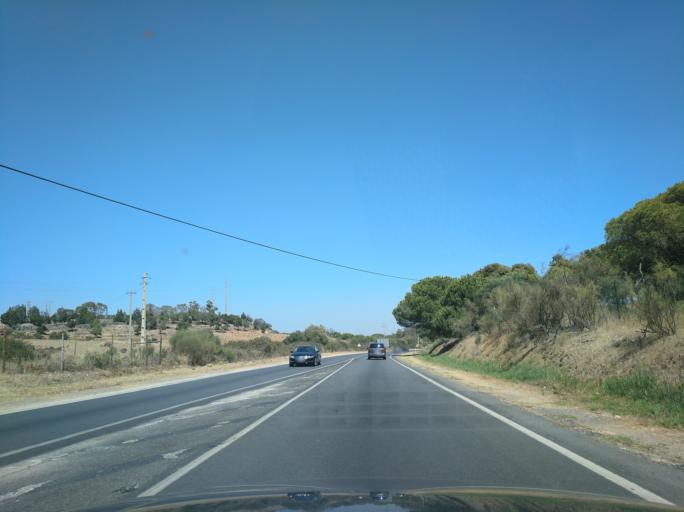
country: PT
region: Faro
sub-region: Vila Real de Santo Antonio
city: Monte Gordo
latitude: 37.1844
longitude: -7.4828
